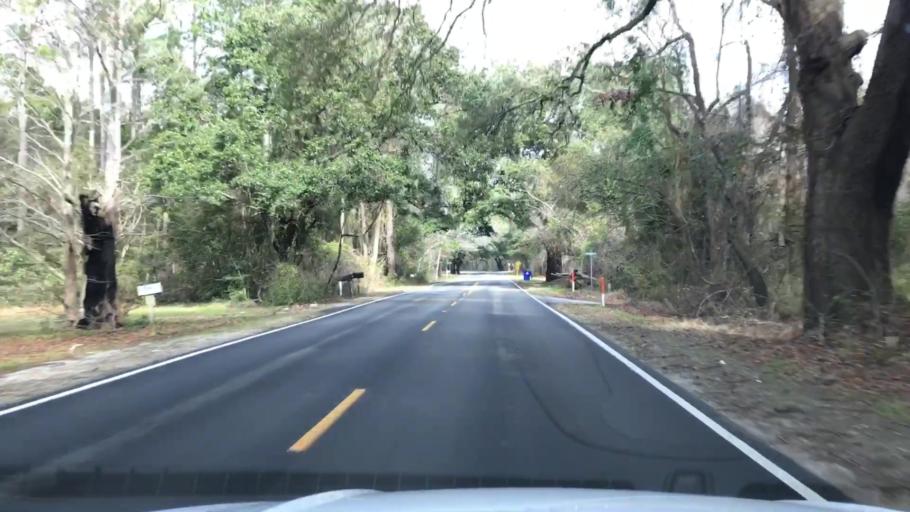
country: US
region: South Carolina
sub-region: Charleston County
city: Folly Beach
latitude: 32.6967
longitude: -80.0151
